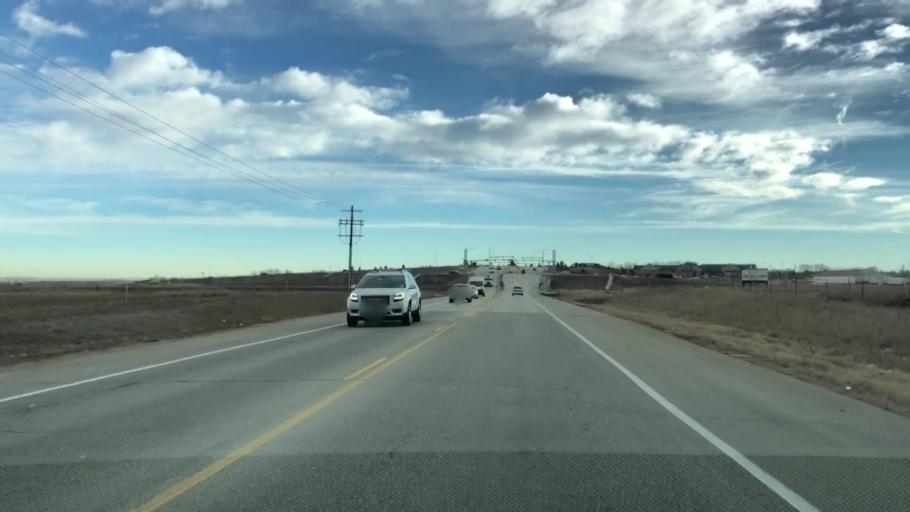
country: US
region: Colorado
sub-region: Weld County
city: Windsor
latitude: 40.4795
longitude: -104.9994
